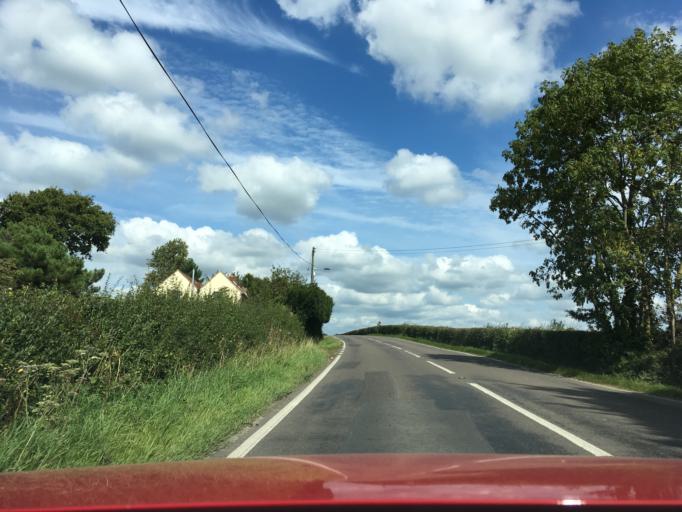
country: GB
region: England
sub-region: South Gloucestershire
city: Tytherington
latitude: 51.5935
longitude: -2.4461
